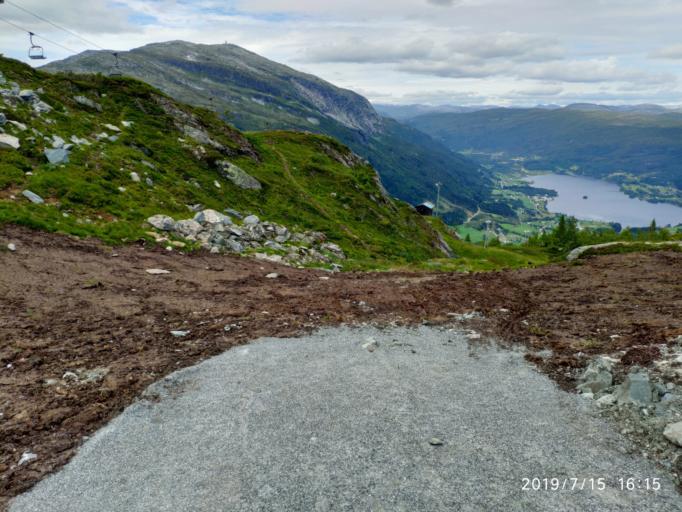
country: NO
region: Hordaland
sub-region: Voss
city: Voss
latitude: 60.6459
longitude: 6.4031
